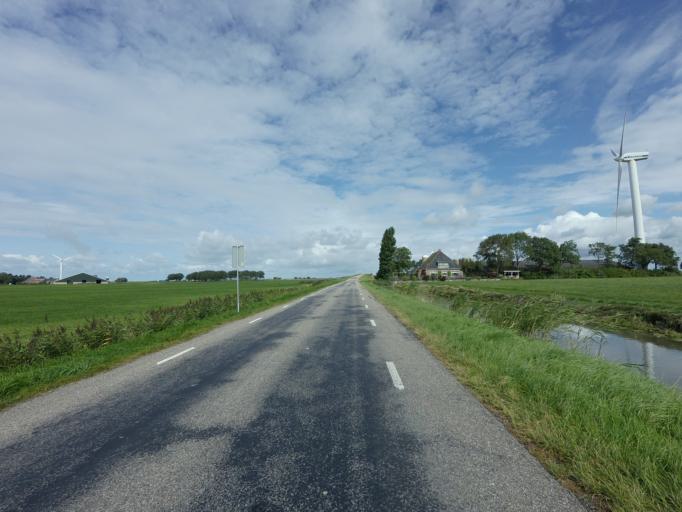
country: NL
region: Friesland
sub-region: Sudwest Fryslan
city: Makkum
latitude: 53.0897
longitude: 5.4209
